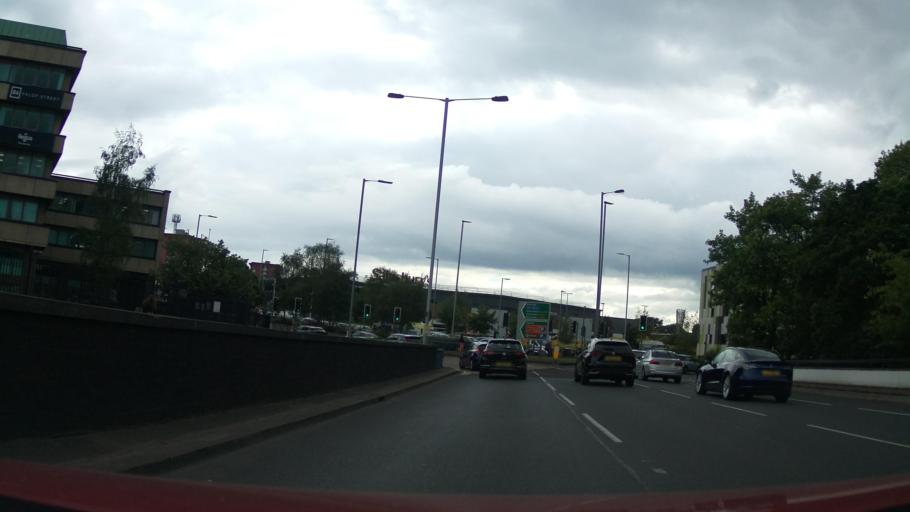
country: GB
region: England
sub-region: Wolverhampton
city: Wolverhampton
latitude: 52.5850
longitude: -2.1344
